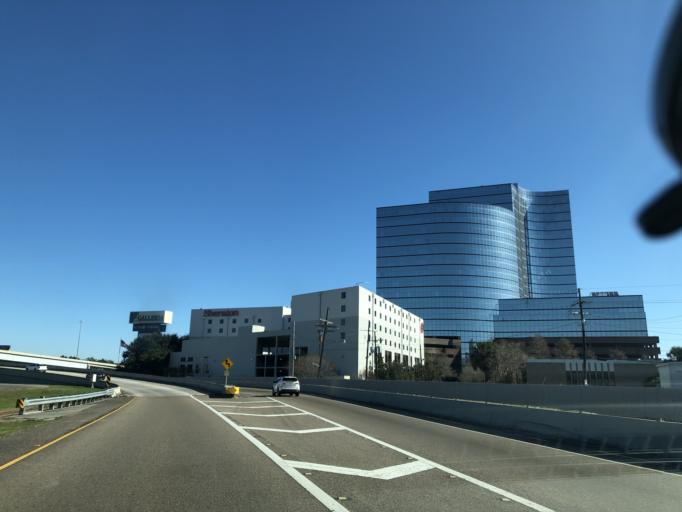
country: US
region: Louisiana
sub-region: Jefferson Parish
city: Metairie
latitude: 29.9953
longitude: -90.1546
